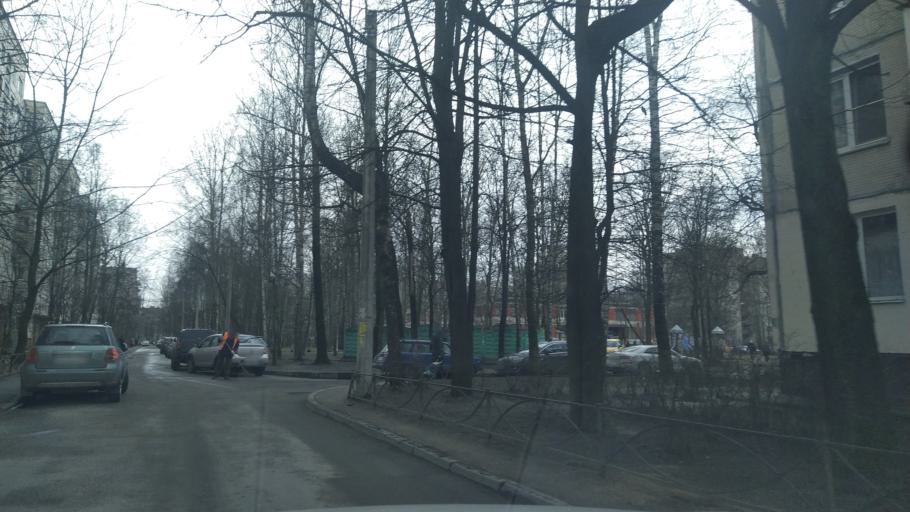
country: RU
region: St.-Petersburg
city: Grazhdanka
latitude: 60.0463
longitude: 30.3949
